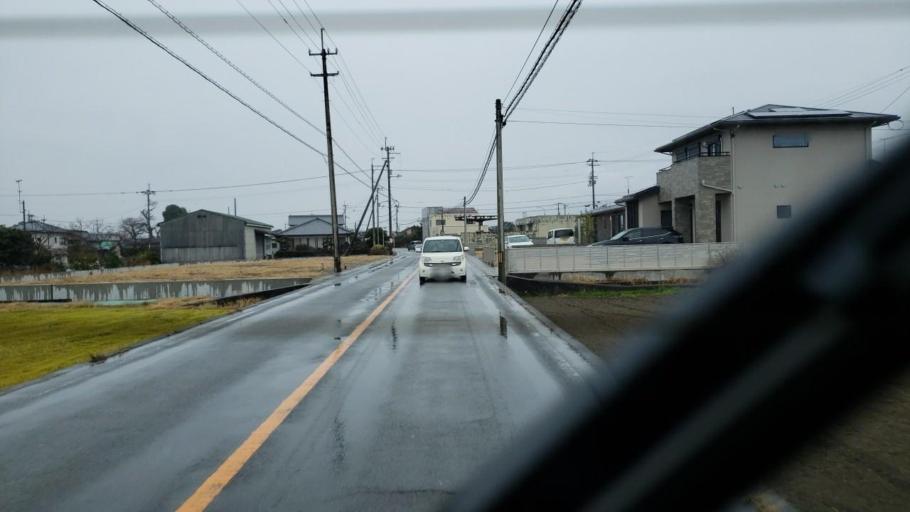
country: JP
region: Tokushima
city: Kamojimacho-jogejima
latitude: 34.0971
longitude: 134.3585
